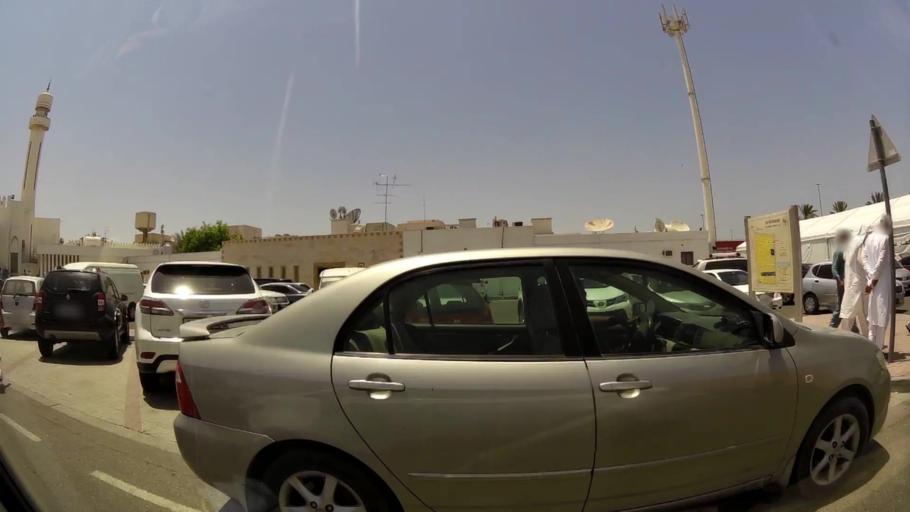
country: AE
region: Ash Shariqah
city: Sharjah
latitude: 25.2969
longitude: 55.3364
